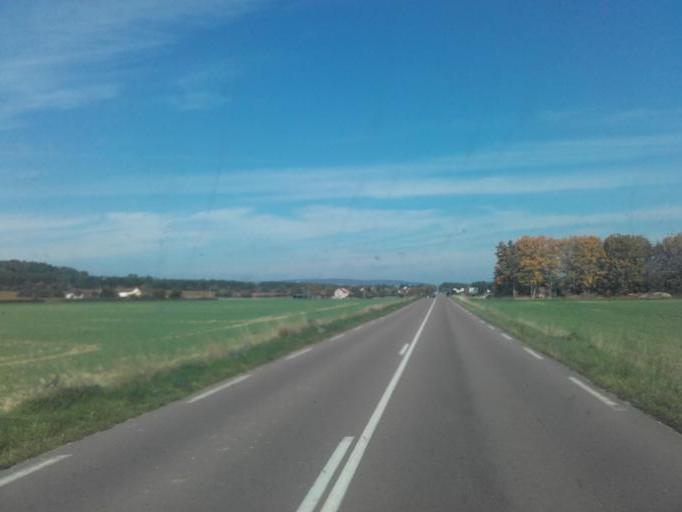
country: FR
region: Bourgogne
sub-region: Departement de Saone-et-Loire
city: Rully
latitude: 46.8866
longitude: 4.7523
